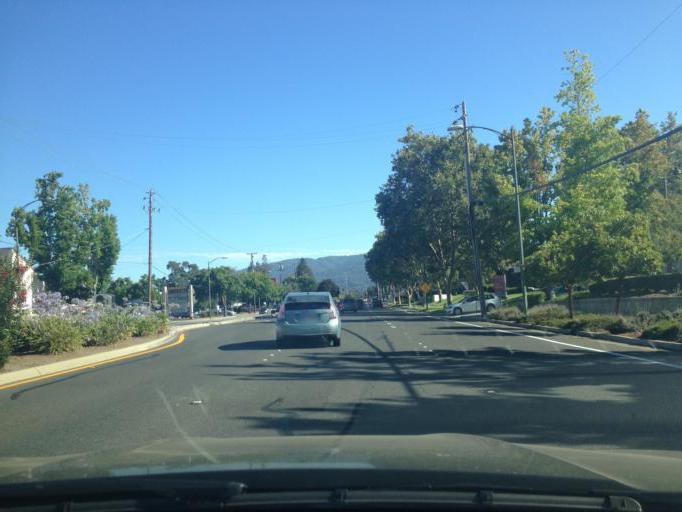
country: US
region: California
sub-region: Santa Clara County
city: Cupertino
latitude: 37.2968
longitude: -122.0323
